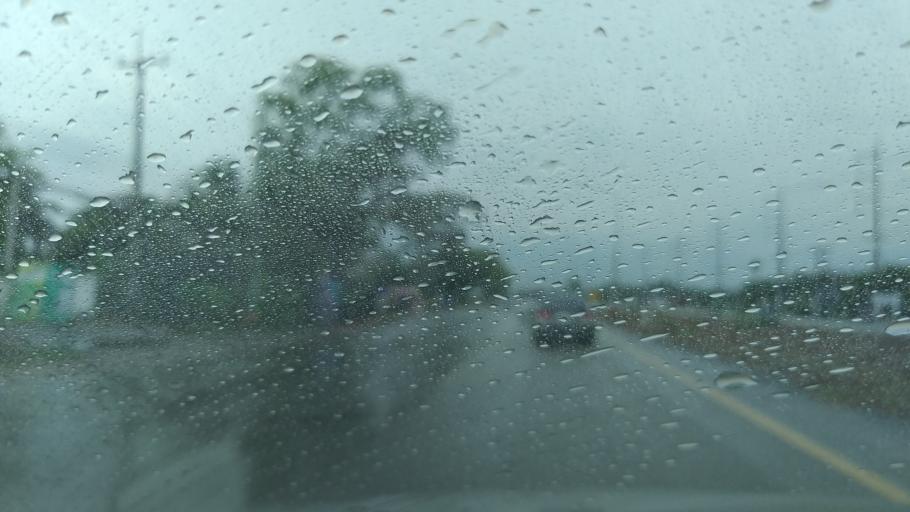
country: TH
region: Trat
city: Khao Saming
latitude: 12.3958
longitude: 102.3564
